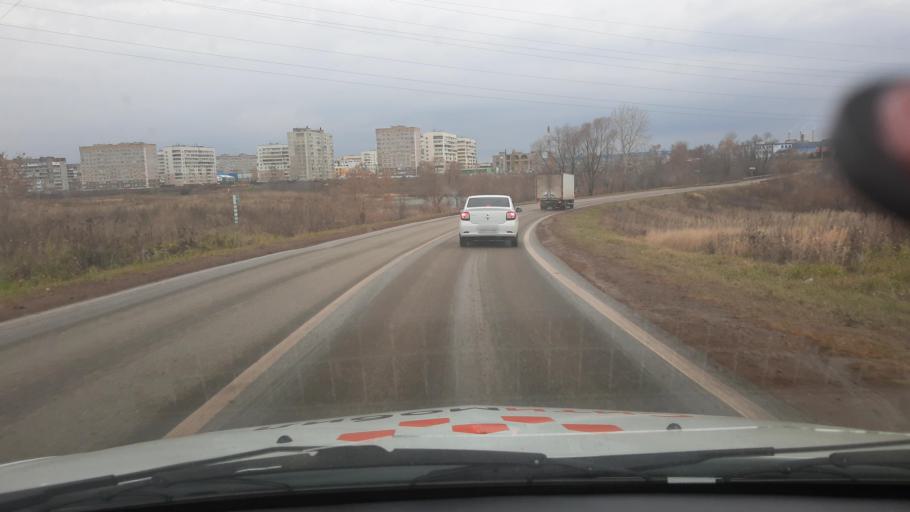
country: RU
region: Bashkortostan
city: Iglino
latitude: 54.7506
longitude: 56.2501
